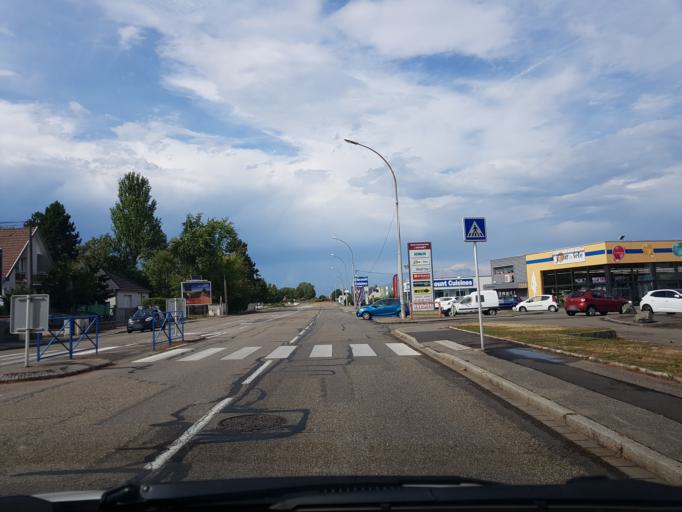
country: FR
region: Alsace
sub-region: Departement du Haut-Rhin
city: Kingersheim
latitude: 47.8029
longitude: 7.3118
